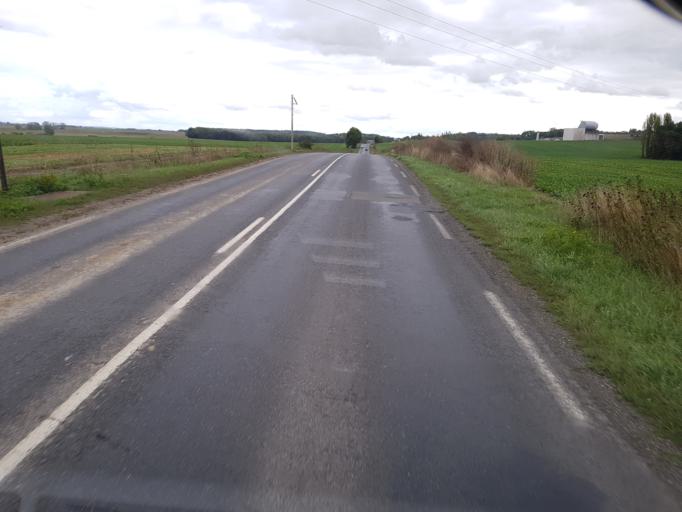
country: FR
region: Ile-de-France
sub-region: Departement de Seine-et-Marne
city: Saint-Soupplets
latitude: 49.0258
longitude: 2.8168
